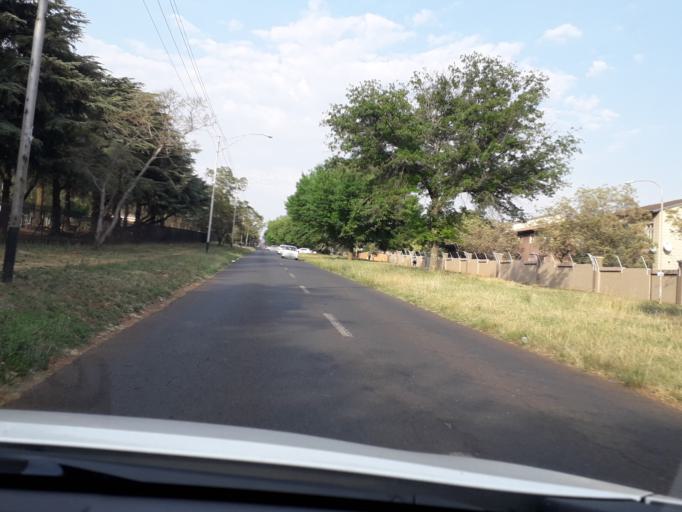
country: ZA
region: Gauteng
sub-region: City of Johannesburg Metropolitan Municipality
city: Johannesburg
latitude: -26.1610
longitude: 27.9878
